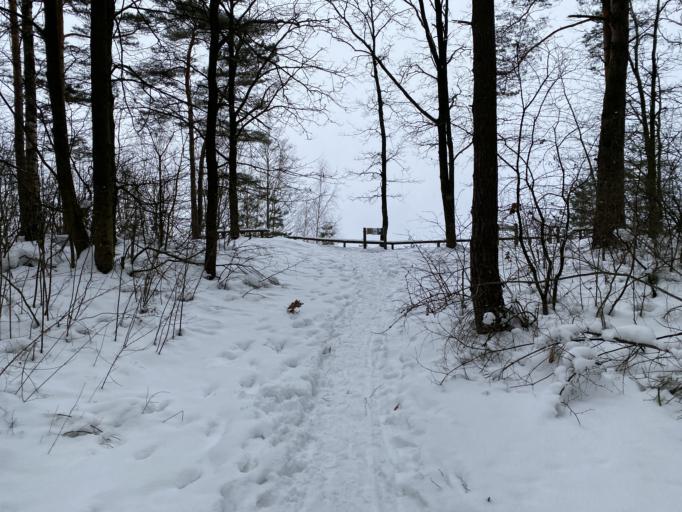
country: LT
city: Ramuciai
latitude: 54.8830
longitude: 24.0619
